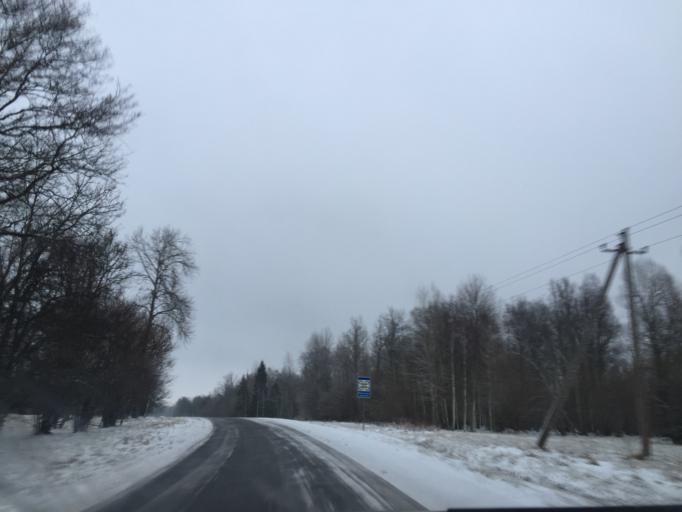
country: EE
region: Laeaene
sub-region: Lihula vald
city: Lihula
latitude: 58.5354
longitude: 24.0641
